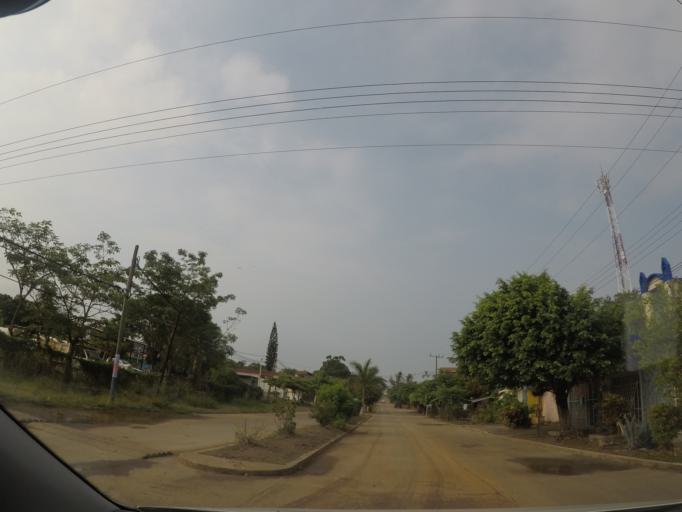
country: MX
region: Oaxaca
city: Matias Romero
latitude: 16.8768
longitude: -95.0475
